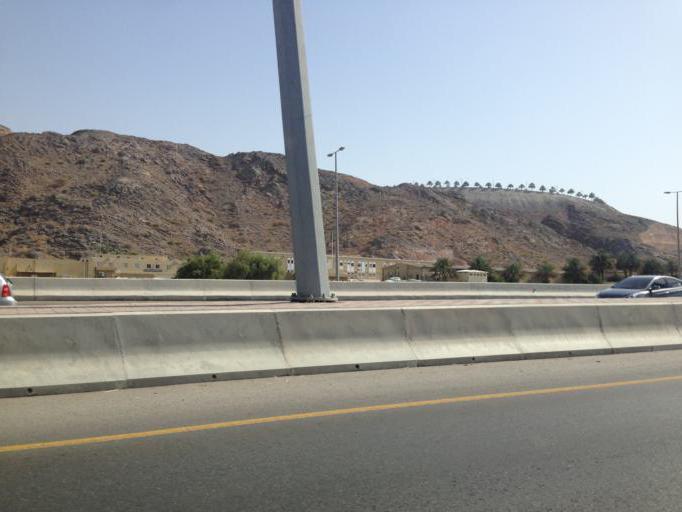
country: OM
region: Muhafazat Masqat
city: Bawshar
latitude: 23.5994
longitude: 58.4835
